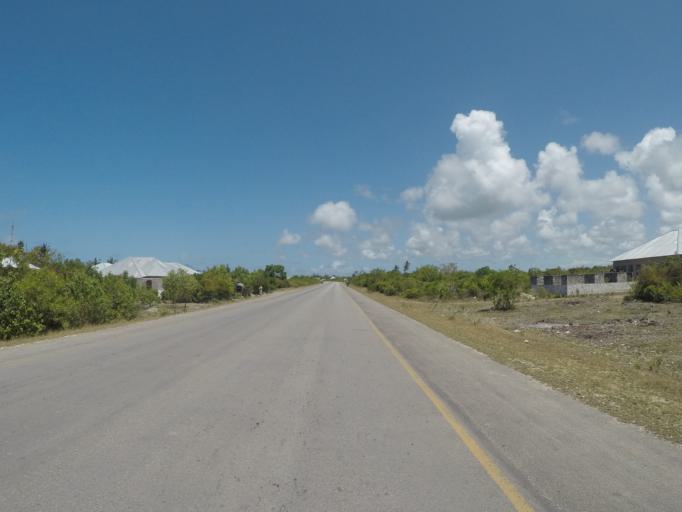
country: TZ
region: Zanzibar Central/South
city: Nganane
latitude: -6.3136
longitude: 39.5419
